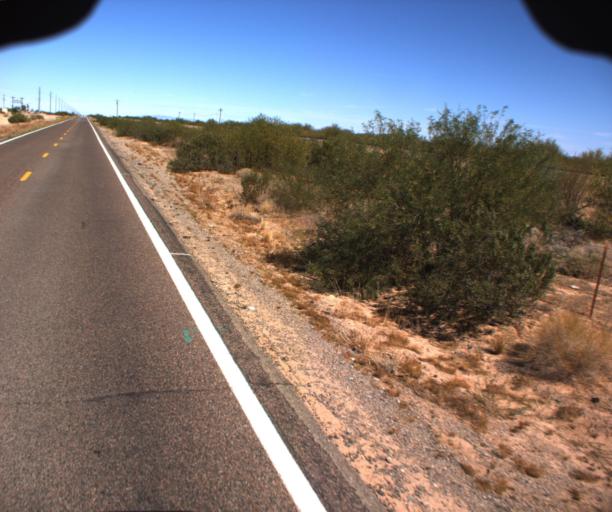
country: US
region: Arizona
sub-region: La Paz County
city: Salome
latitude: 33.8489
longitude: -113.9013
